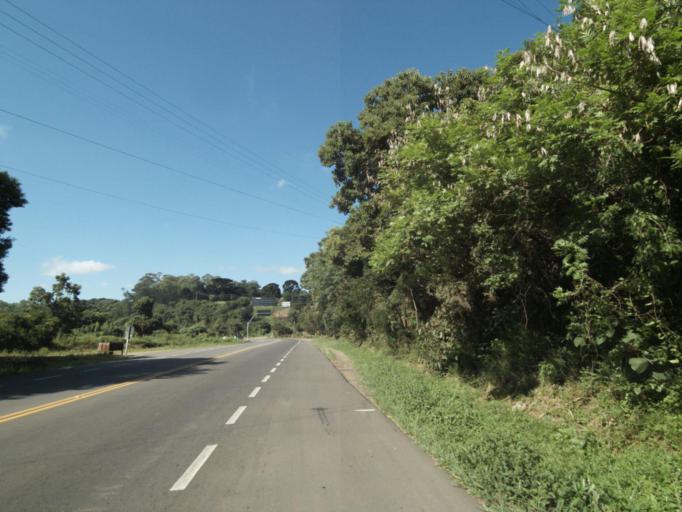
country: BR
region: Rio Grande do Sul
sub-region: Bento Goncalves
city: Bento Goncalves
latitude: -29.1211
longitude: -51.5434
